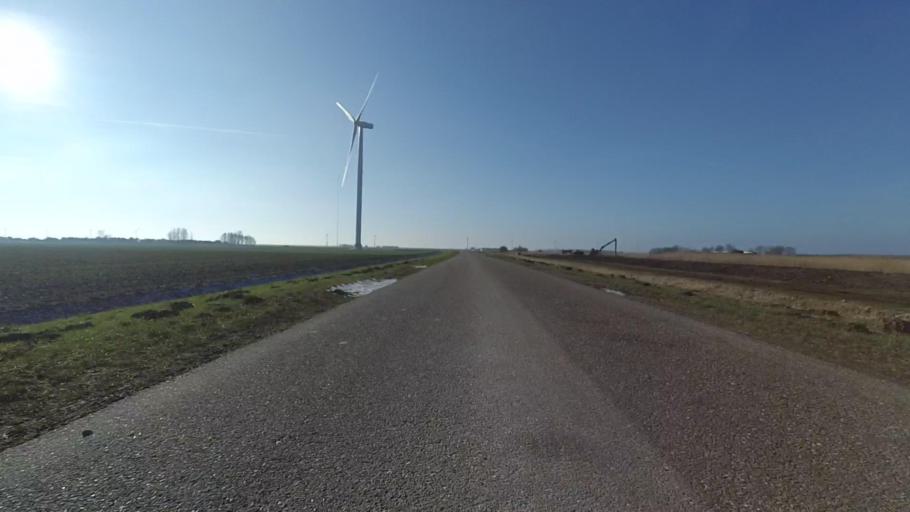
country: NL
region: Utrecht
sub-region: Gemeente Bunschoten
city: Spakenburg
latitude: 52.3034
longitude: 5.3647
